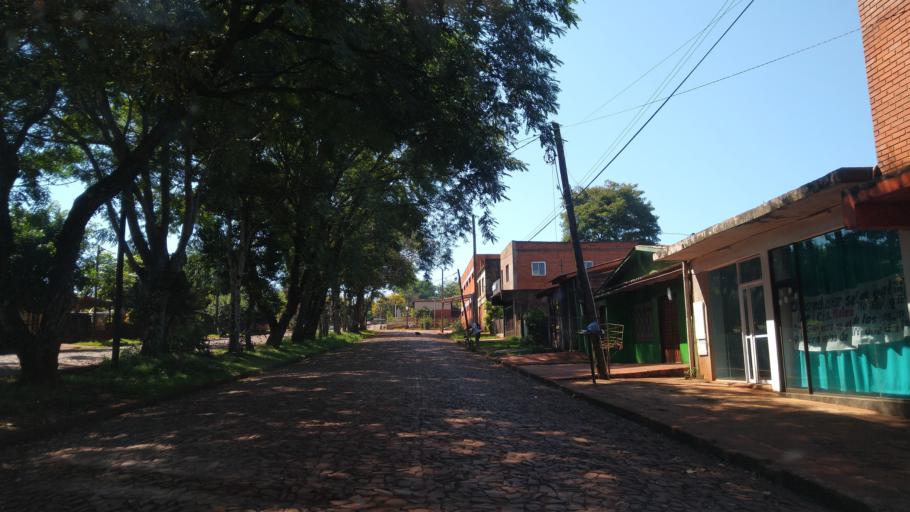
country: AR
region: Misiones
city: Puerto Libertad
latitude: -25.9686
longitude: -54.5618
